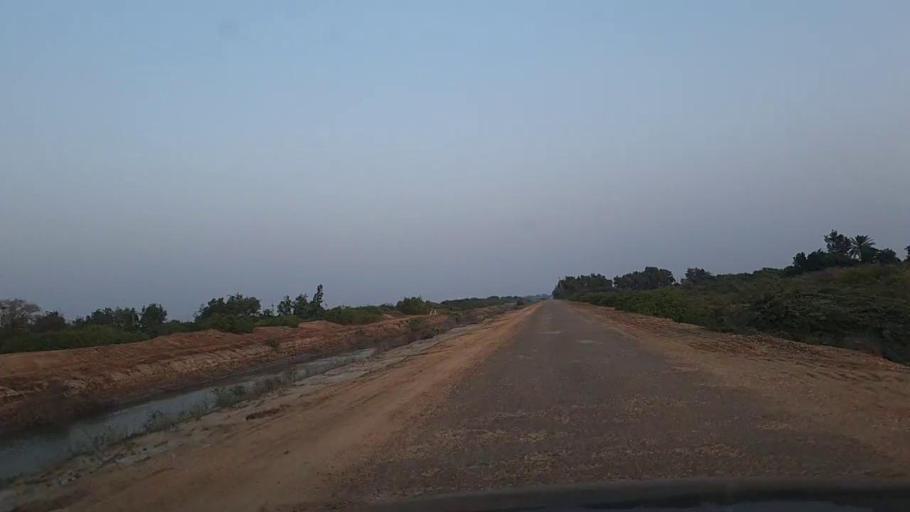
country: PK
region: Sindh
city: Mirpur Sakro
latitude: 24.6323
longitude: 67.6257
